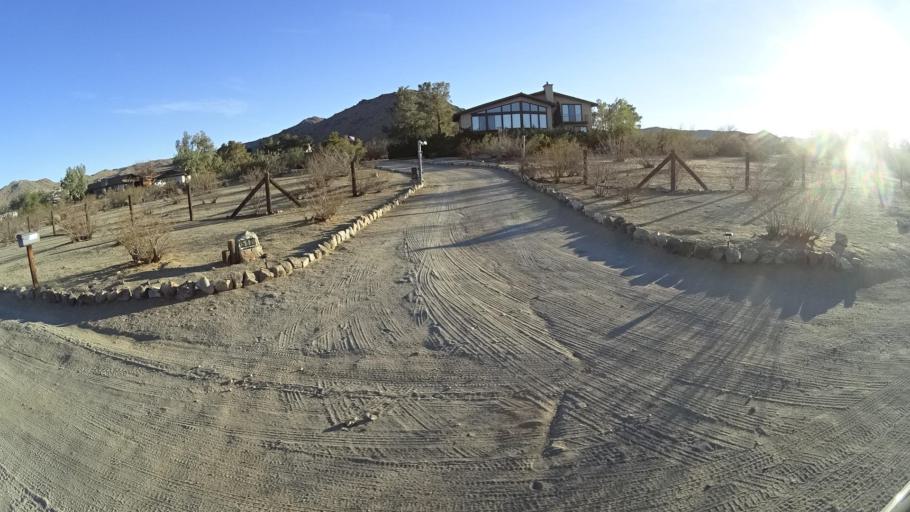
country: US
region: California
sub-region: Kern County
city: Ridgecrest
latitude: 35.5825
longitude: -117.6606
